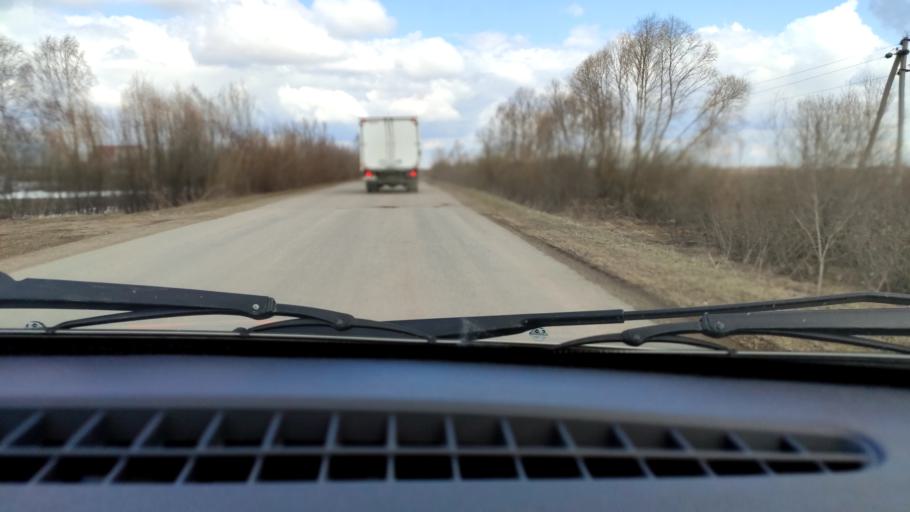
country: RU
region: Bashkortostan
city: Kudeyevskiy
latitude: 54.8311
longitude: 56.7930
